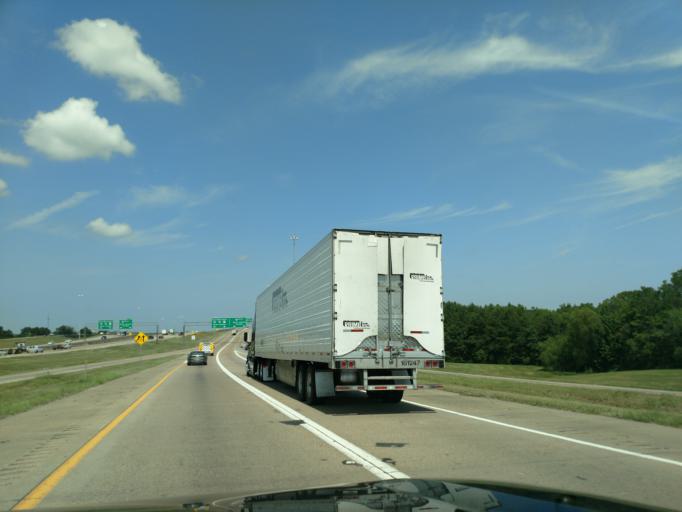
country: US
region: Mississippi
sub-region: Rankin County
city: Pearl
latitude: 32.2741
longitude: -90.1595
